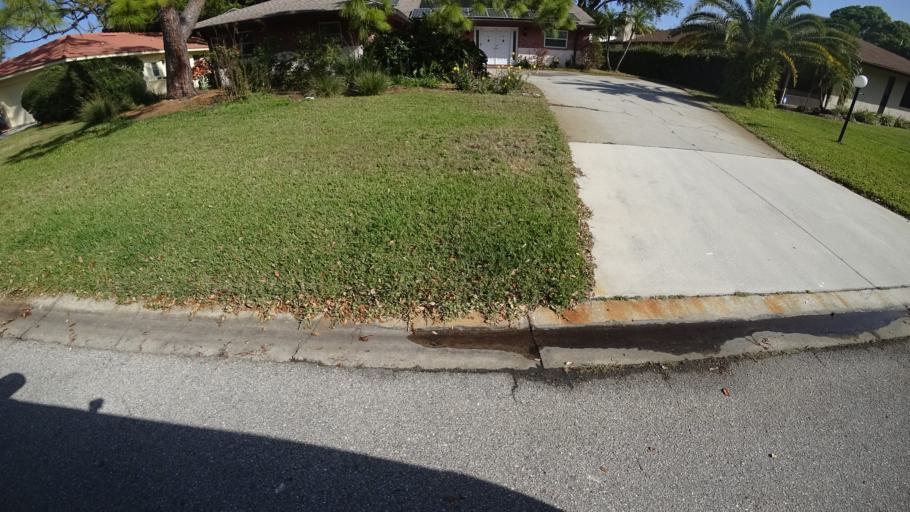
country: US
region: Florida
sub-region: Manatee County
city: Whitfield
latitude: 27.4151
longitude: -82.5579
